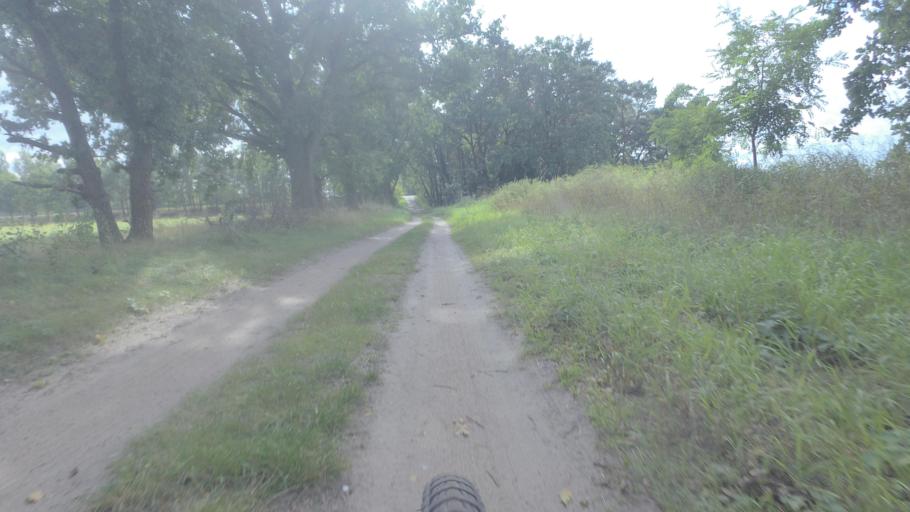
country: DE
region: Brandenburg
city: Ludwigsfelde
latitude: 52.3205
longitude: 13.2043
